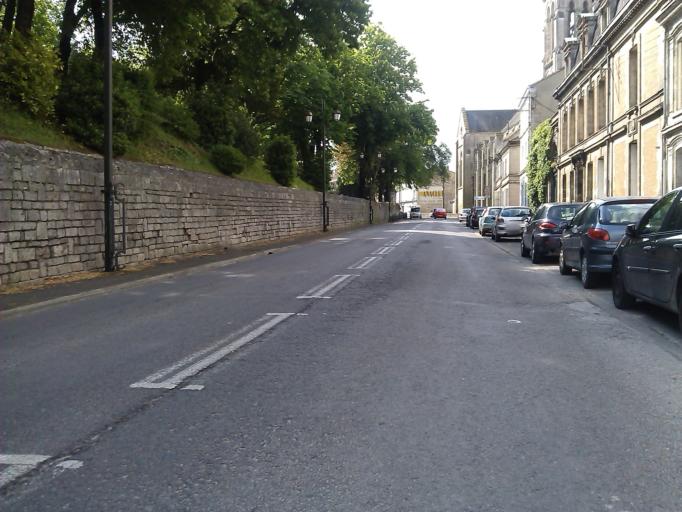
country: FR
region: Poitou-Charentes
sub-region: Departement de la Charente
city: Angouleme
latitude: 45.6516
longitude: 0.1454
